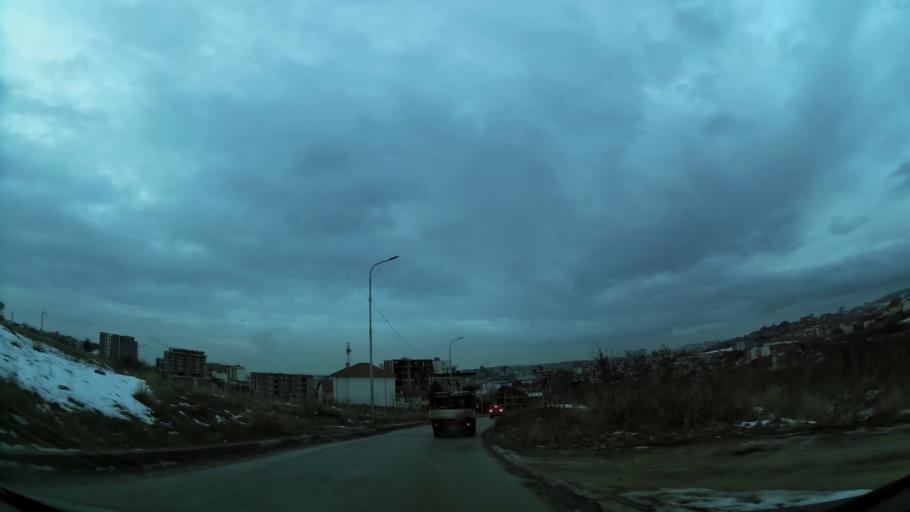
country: XK
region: Pristina
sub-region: Komuna e Prishtines
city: Pristina
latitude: 42.6369
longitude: 21.1653
